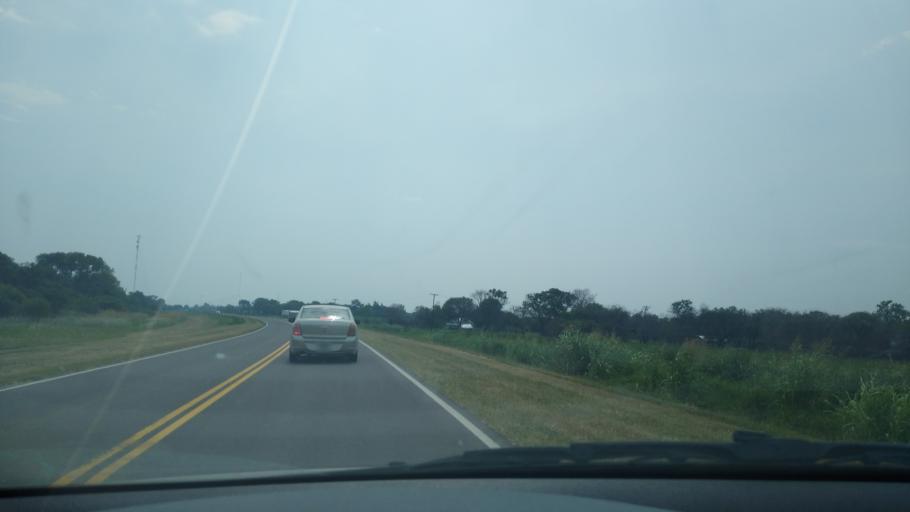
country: AR
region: Chaco
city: La Eduvigis
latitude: -26.8404
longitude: -59.0559
